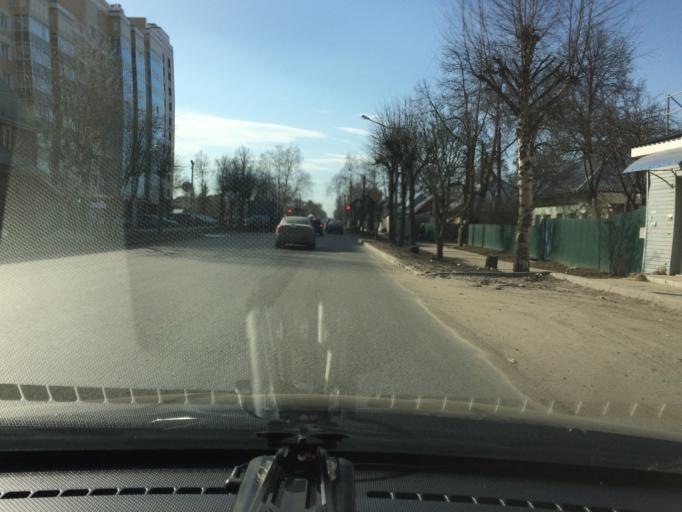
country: RU
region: Mariy-El
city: Yoshkar-Ola
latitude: 56.6498
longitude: 47.8973
